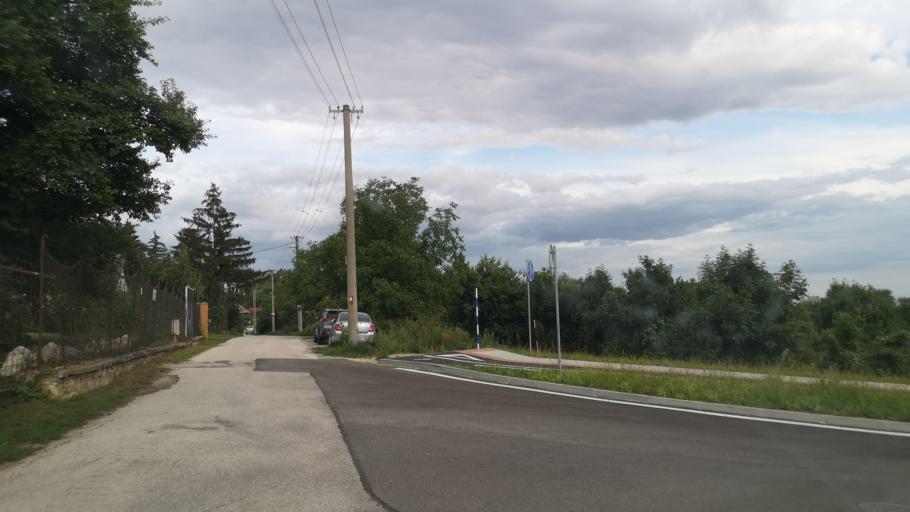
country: SK
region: Nitriansky
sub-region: Okres Nitra
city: Nitra
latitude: 48.3361
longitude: 18.0812
